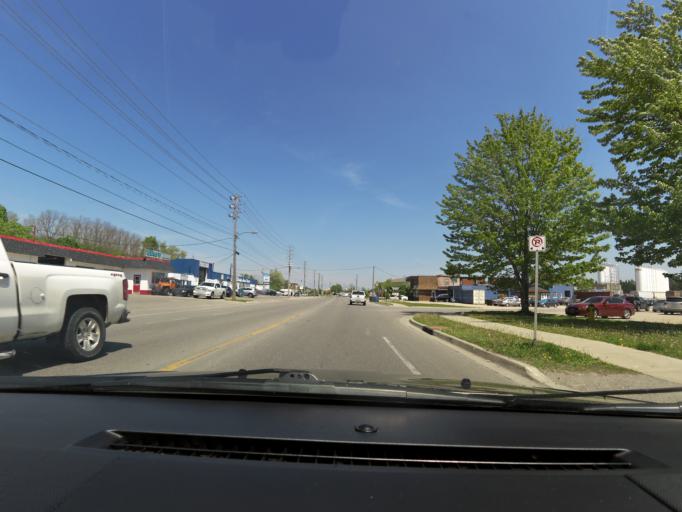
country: CA
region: Ontario
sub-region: Wellington County
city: Guelph
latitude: 43.5549
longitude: -80.2322
